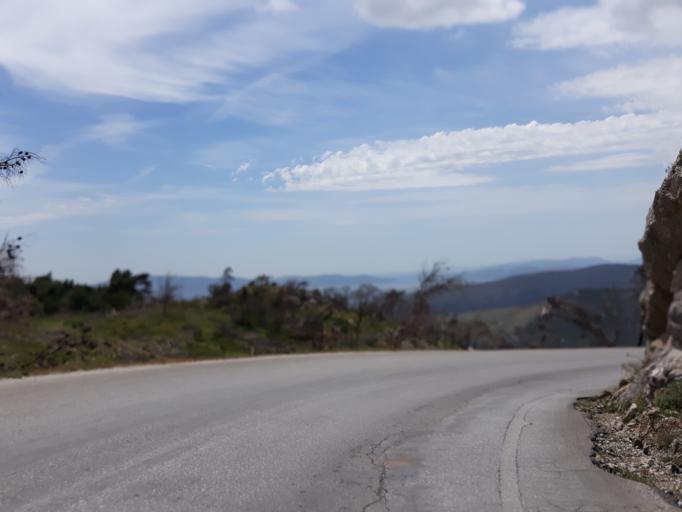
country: GR
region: Attica
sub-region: Nomarchia Dytikis Attikis
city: Magoula
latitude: 38.1555
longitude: 23.5270
